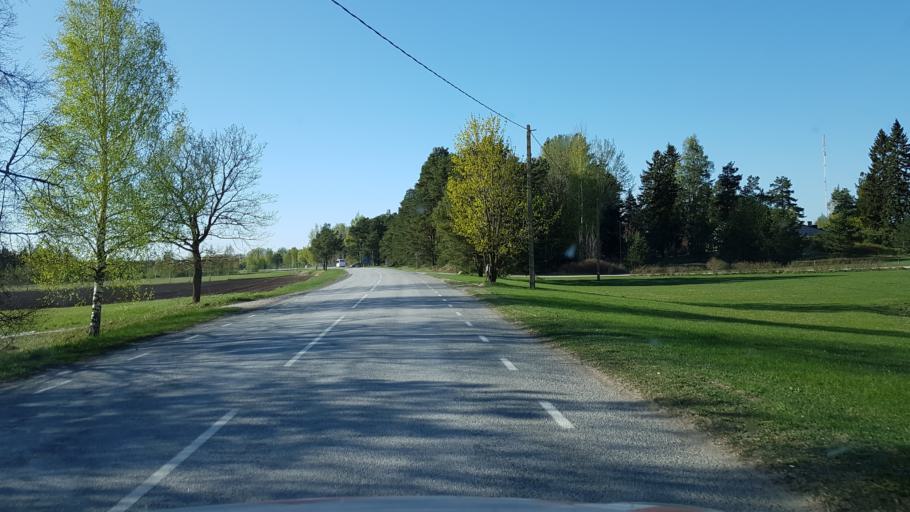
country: EE
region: Paernumaa
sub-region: Paikuse vald
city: Paikuse
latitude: 58.3548
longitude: 24.6640
